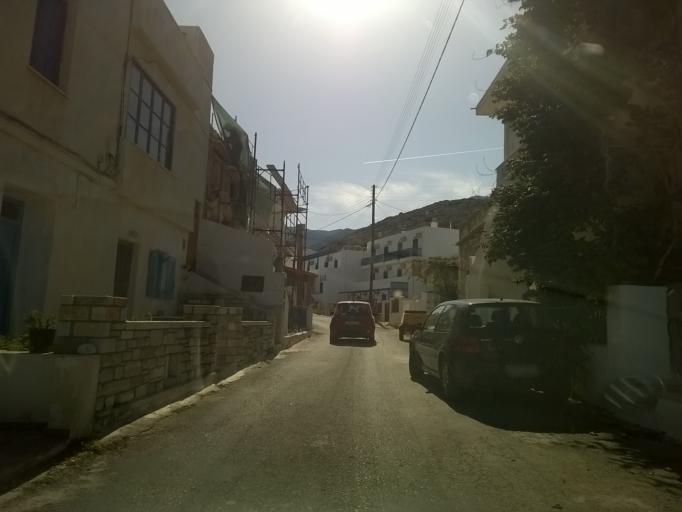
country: GR
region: South Aegean
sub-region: Nomos Kykladon
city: Filotion
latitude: 37.1810
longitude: 25.5512
